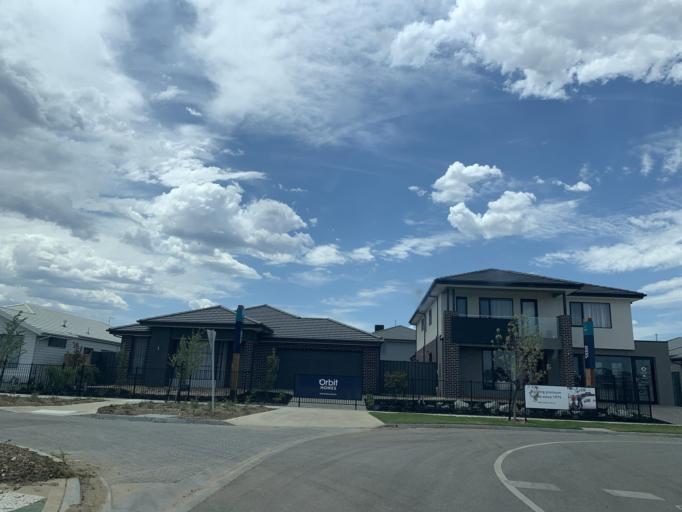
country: AU
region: Victoria
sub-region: Cardinia
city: Officer South
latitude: -38.1222
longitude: 145.3685
